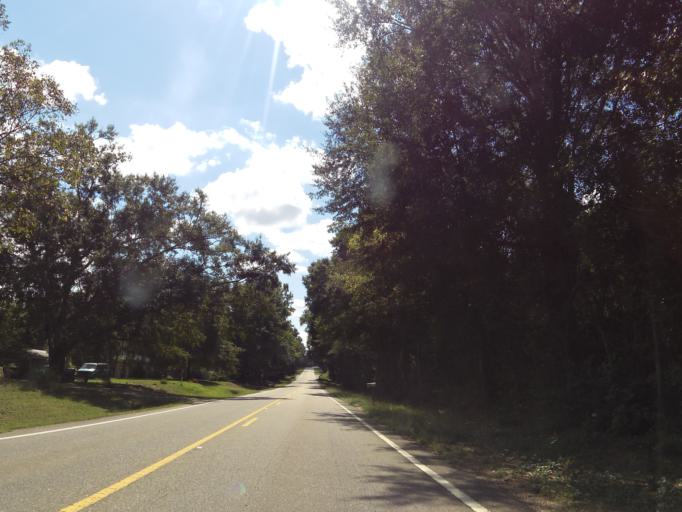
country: US
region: Alabama
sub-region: Dallas County
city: Selma
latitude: 32.4747
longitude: -87.0927
